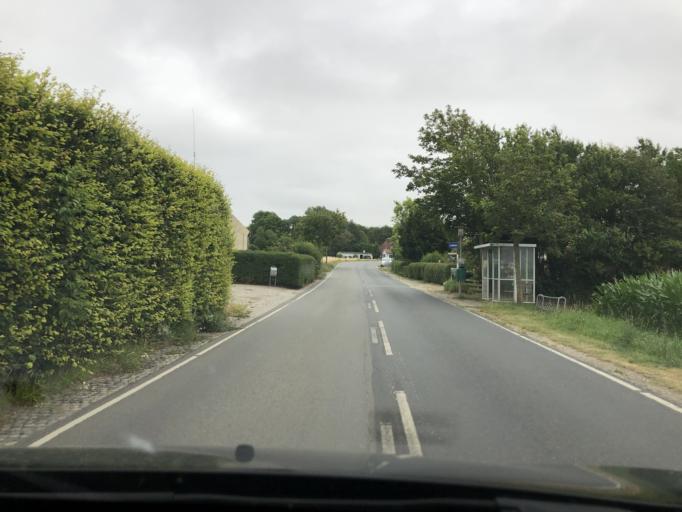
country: DK
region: South Denmark
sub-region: AEro Kommune
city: AEroskobing
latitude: 54.9142
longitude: 10.2847
